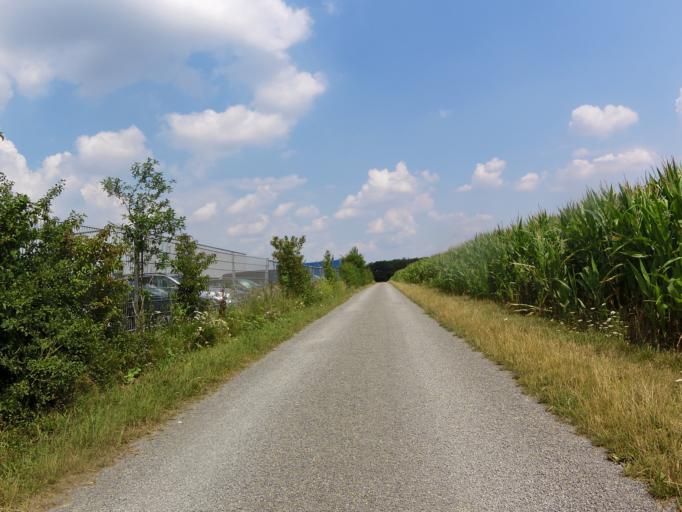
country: DE
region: Bavaria
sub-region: Regierungsbezirk Unterfranken
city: Eibelstadt
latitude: 49.7304
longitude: 9.9708
